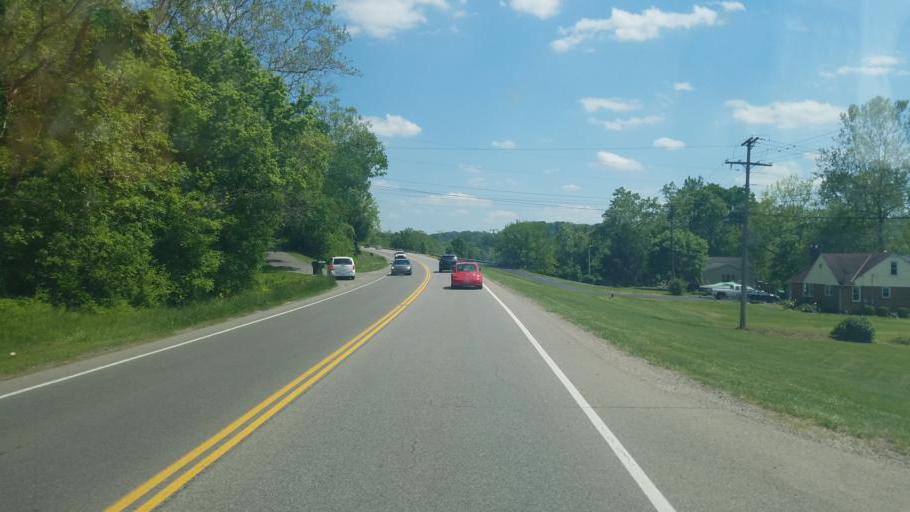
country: US
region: Ohio
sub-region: Muskingum County
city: Zanesville
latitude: 39.9680
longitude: -82.0517
